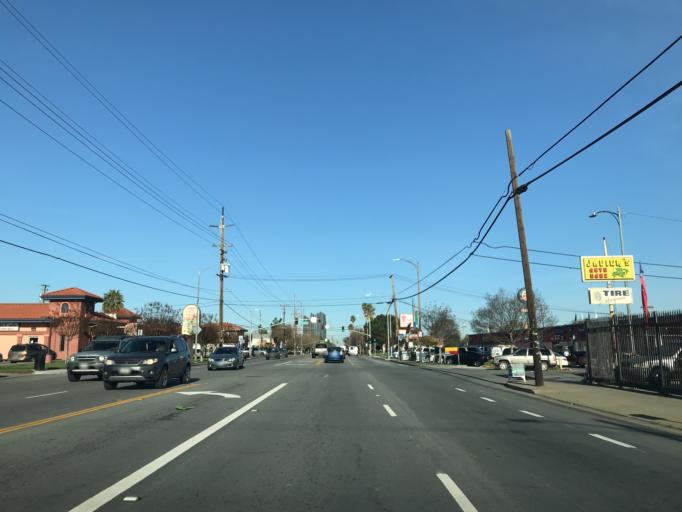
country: US
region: California
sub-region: Santa Clara County
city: Alum Rock
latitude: 37.3446
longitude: -121.8476
